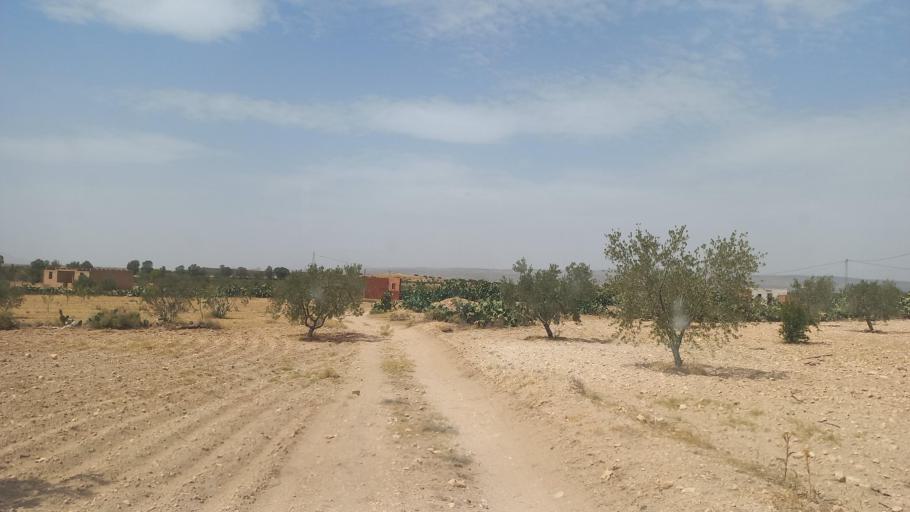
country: TN
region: Al Qasrayn
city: Kasserine
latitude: 35.2644
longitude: 8.9853
